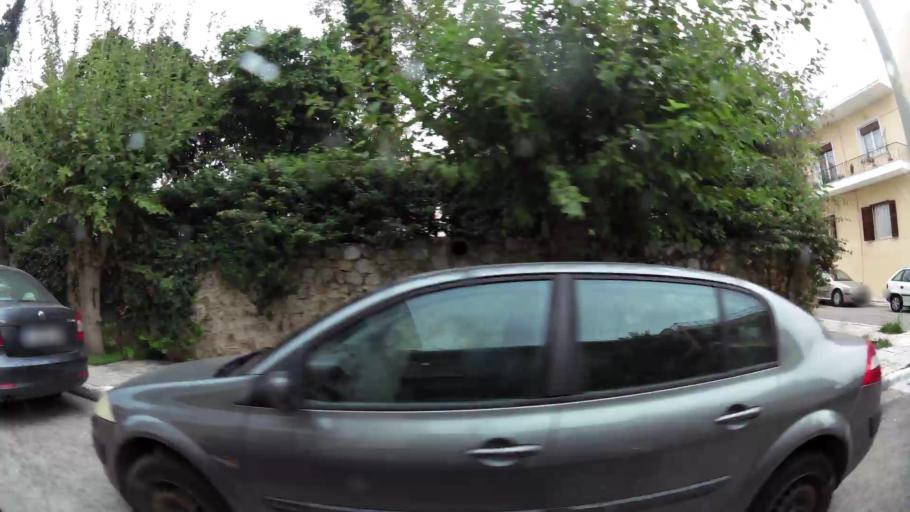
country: GR
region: Attica
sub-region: Nomarchia Athinas
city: Chaidari
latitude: 38.0044
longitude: 23.6584
